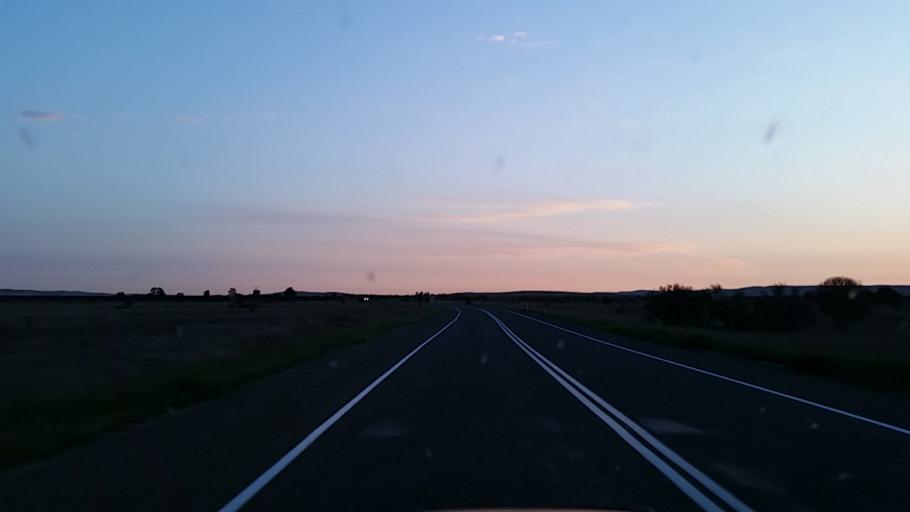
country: AU
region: South Australia
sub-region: Peterborough
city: Peterborough
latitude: -33.1547
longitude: 138.9217
